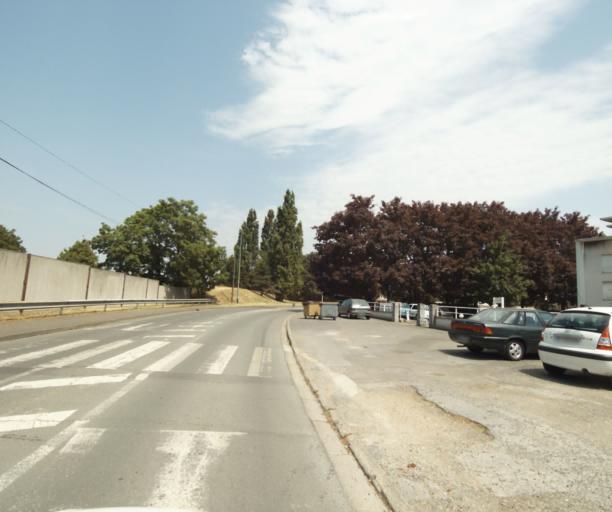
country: FR
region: Ile-de-France
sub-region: Departement des Yvelines
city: Conflans-Sainte-Honorine
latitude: 48.9979
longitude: 2.0811
